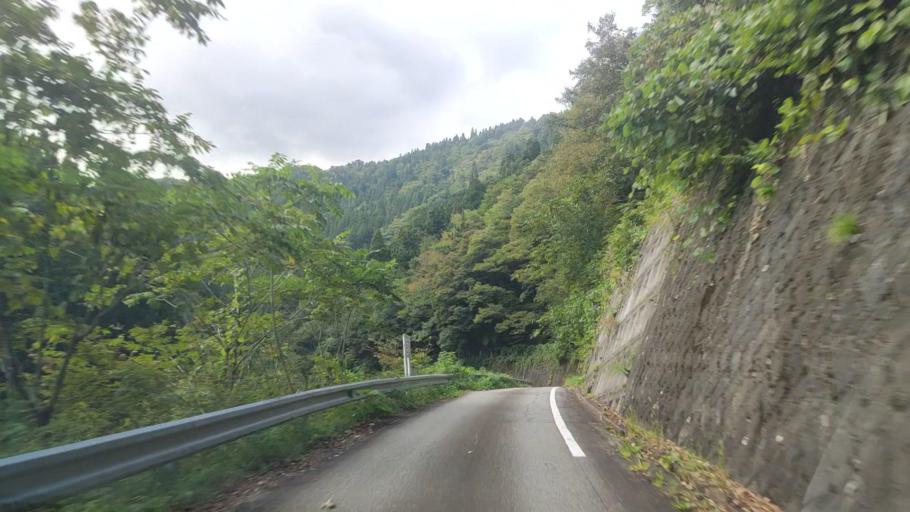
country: JP
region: Gifu
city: Takayama
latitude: 36.3122
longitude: 137.0932
